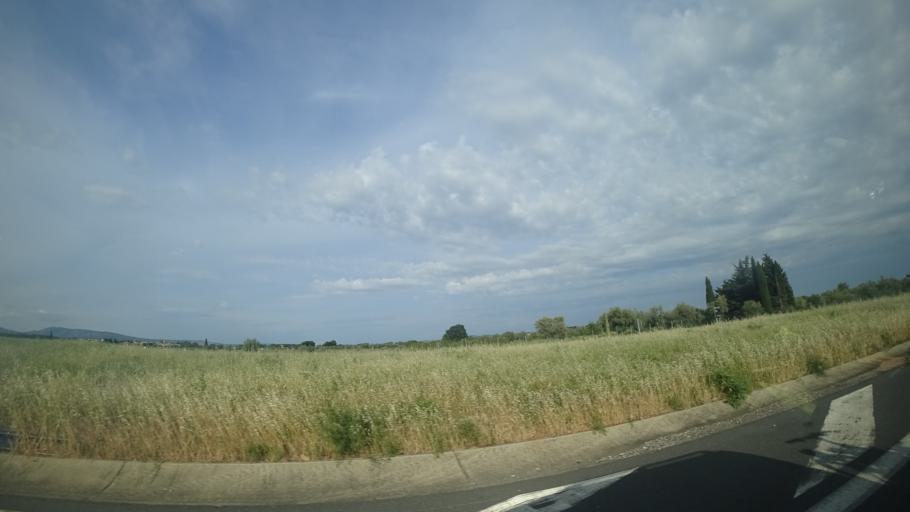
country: FR
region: Languedoc-Roussillon
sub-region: Departement de l'Herault
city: Nebian
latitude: 43.6529
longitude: 3.4485
